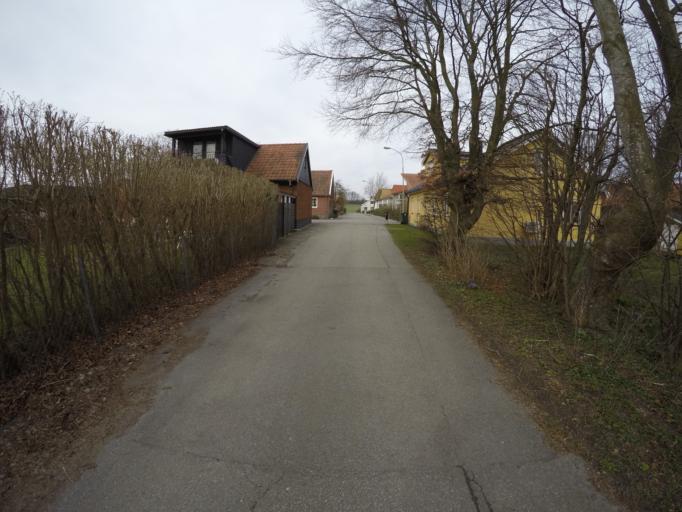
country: SE
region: Skane
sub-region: Ystads Kommun
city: Kopingebro
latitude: 55.4382
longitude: 14.1065
